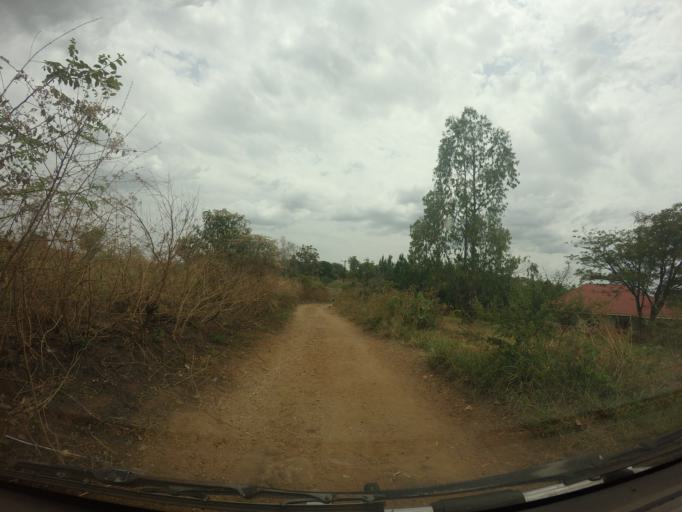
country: UG
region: Northern Region
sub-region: Arua District
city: Arua
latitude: 2.9391
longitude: 30.9397
